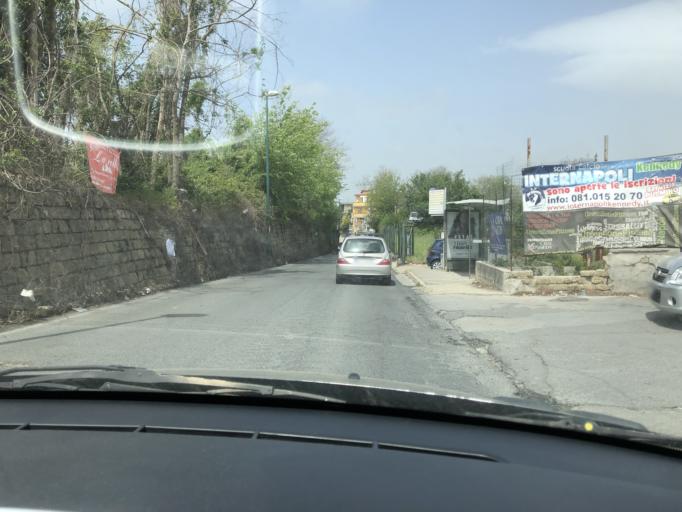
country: IT
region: Campania
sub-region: Provincia di Napoli
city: Torre Caracciolo
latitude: 40.8753
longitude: 14.1865
